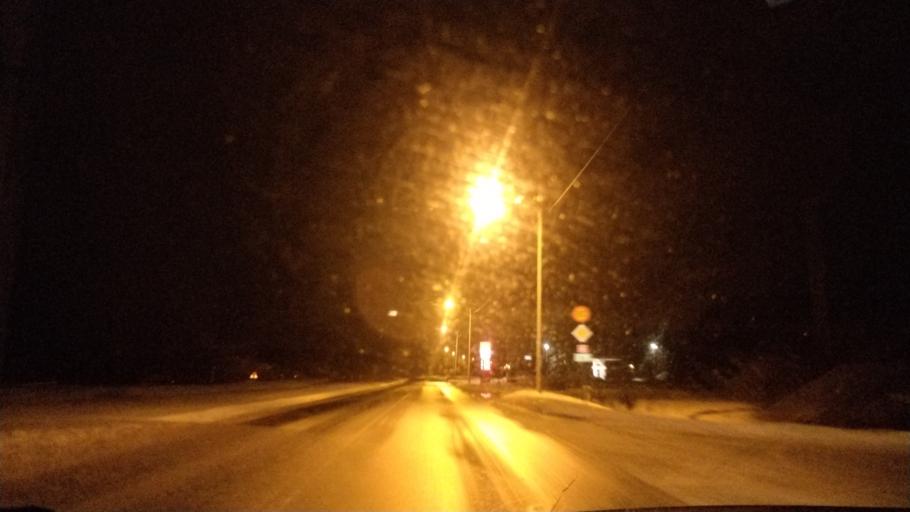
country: FI
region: Lapland
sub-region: Kemi-Tornio
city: Tervola
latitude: 66.1454
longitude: 24.9632
